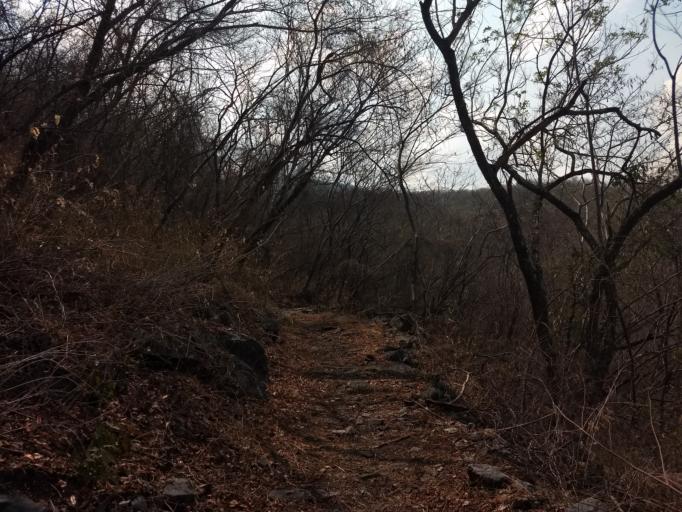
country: MX
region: Morelos
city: La Joya
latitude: 18.6657
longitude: -99.5097
